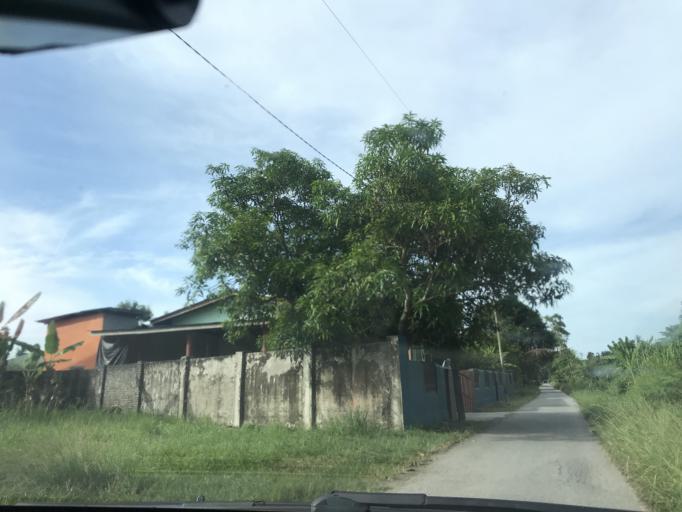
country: MY
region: Kelantan
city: Kota Bharu
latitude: 6.1329
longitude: 102.2172
